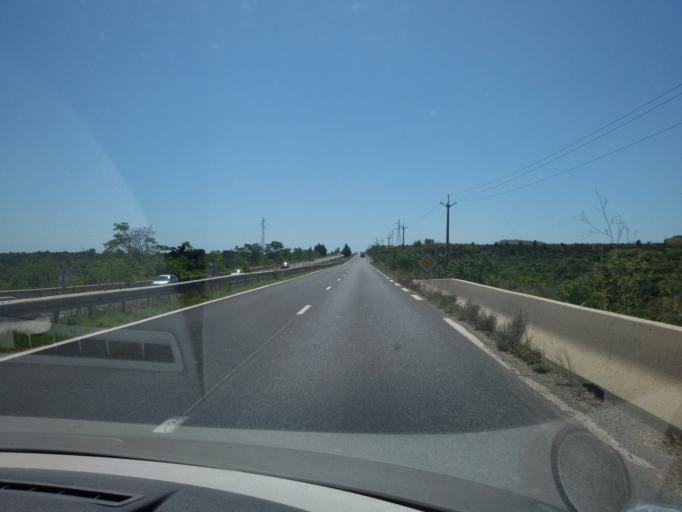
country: FR
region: Languedoc-Roussillon
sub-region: Departement de l'Herault
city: Saint-Jean-de-Vedas
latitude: 43.5431
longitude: 3.8229
